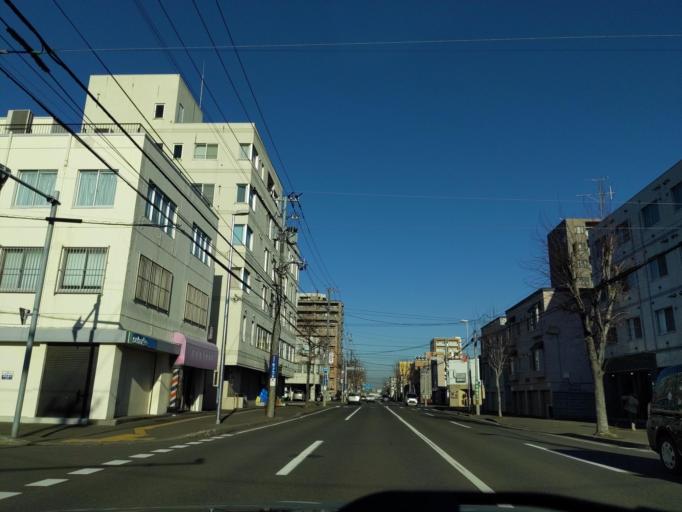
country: JP
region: Hokkaido
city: Sapporo
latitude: 43.0673
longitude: 141.3246
